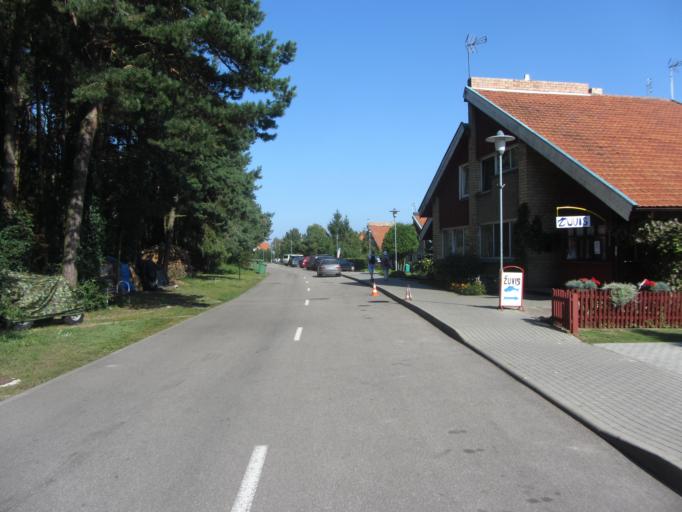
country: LT
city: Neringa
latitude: 55.3744
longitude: 21.0674
